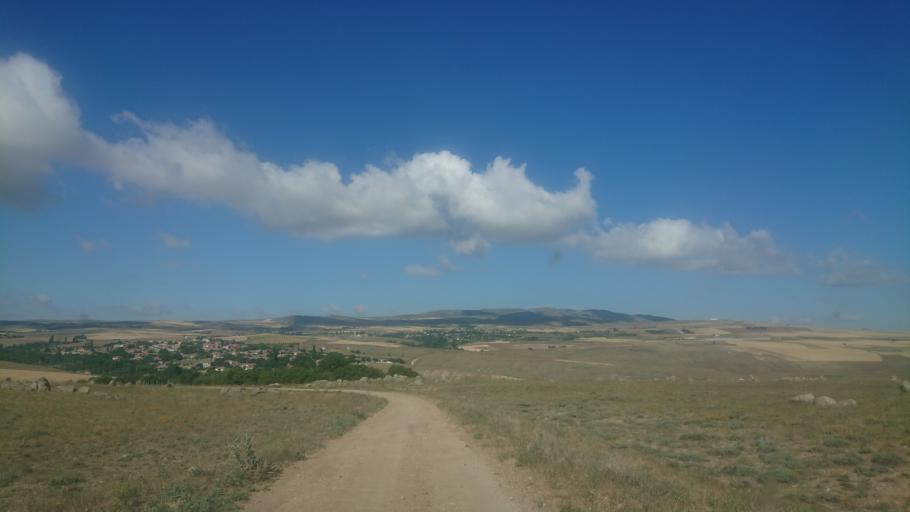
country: TR
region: Aksaray
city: Agacoren
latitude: 38.9097
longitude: 33.8707
